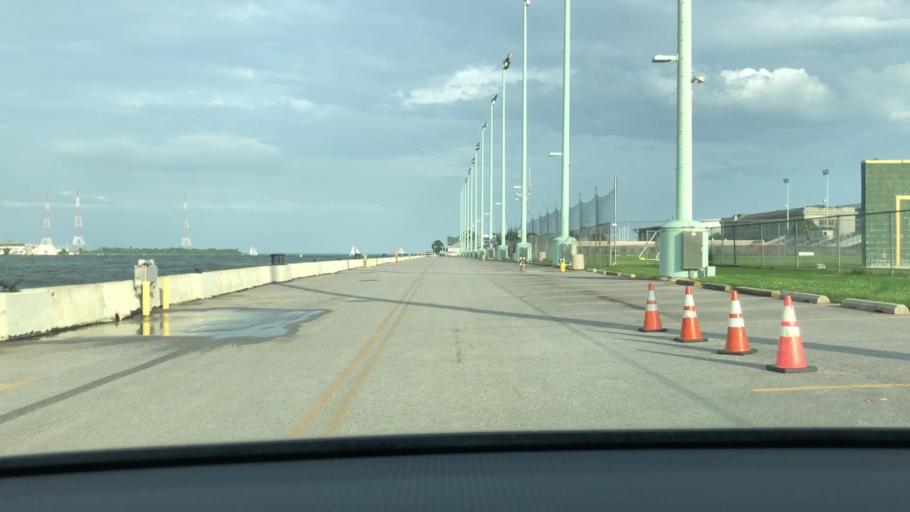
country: US
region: Maryland
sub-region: Anne Arundel County
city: Naval Academy
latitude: 38.9861
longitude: -76.4834
